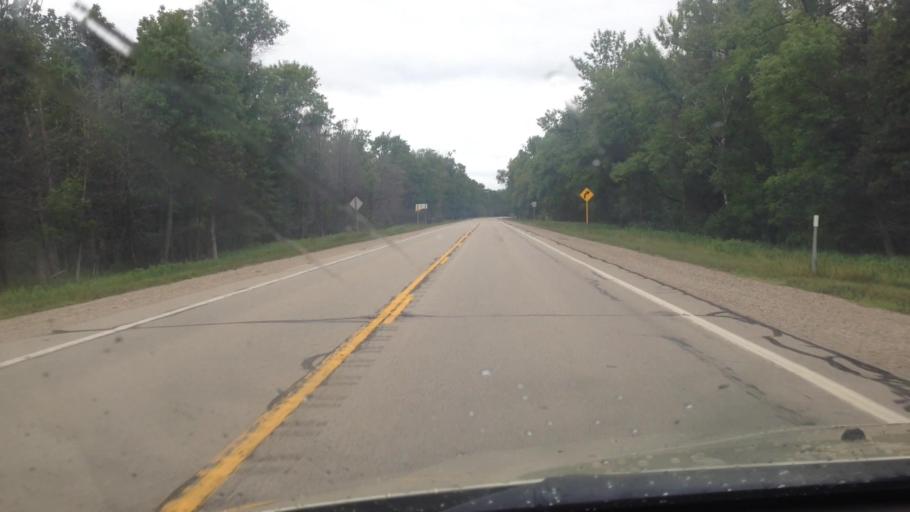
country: US
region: Michigan
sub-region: Menominee County
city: Menominee
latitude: 45.4220
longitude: -87.3480
